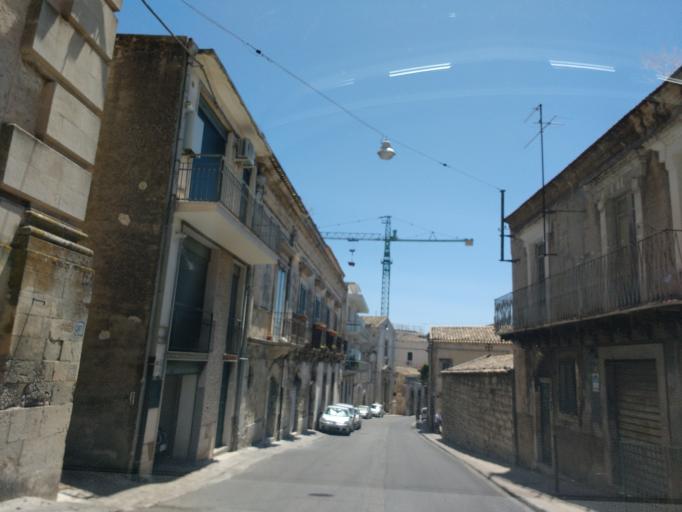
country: IT
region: Sicily
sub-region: Ragusa
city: Modica
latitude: 36.8639
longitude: 14.7622
